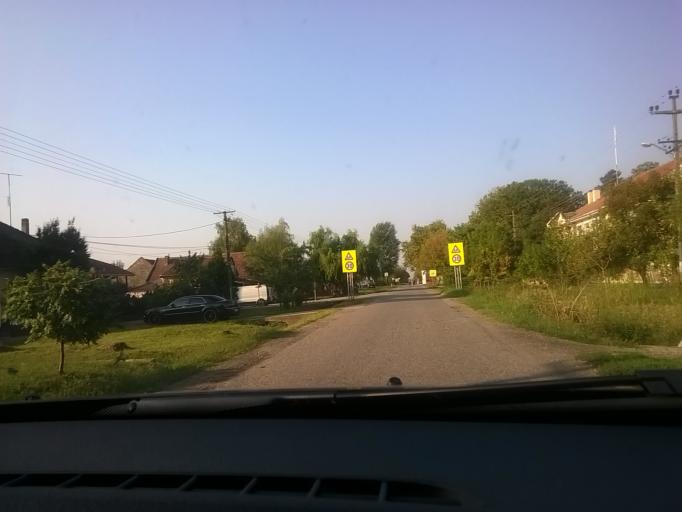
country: RS
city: Pavlis
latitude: 45.1058
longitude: 21.2407
